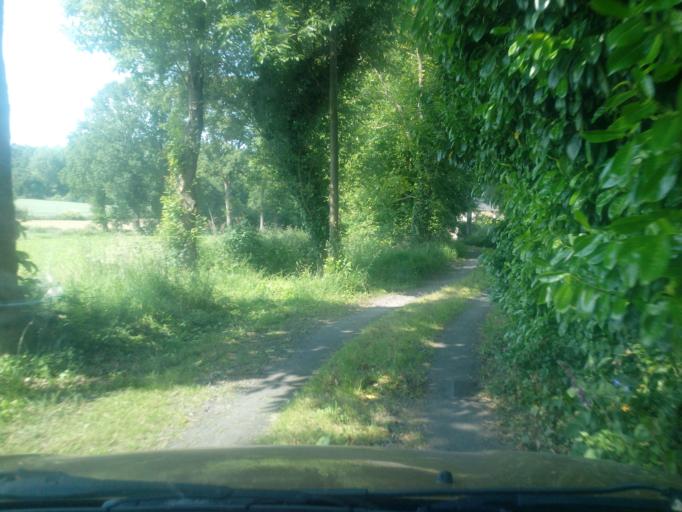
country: FR
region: Brittany
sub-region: Departement d'Ille-et-Vilaine
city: Melesse
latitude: 48.1996
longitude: -1.6799
